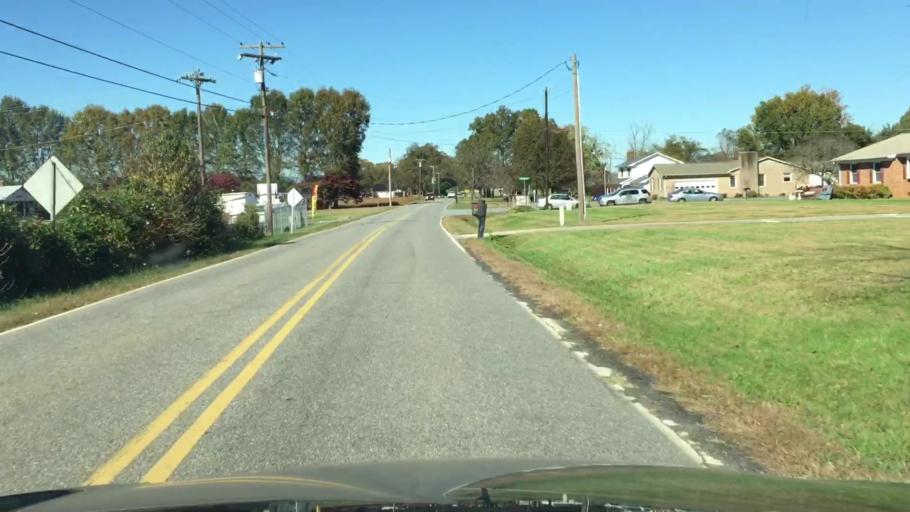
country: US
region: North Carolina
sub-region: Iredell County
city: Mooresville
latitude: 35.5613
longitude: -80.7749
